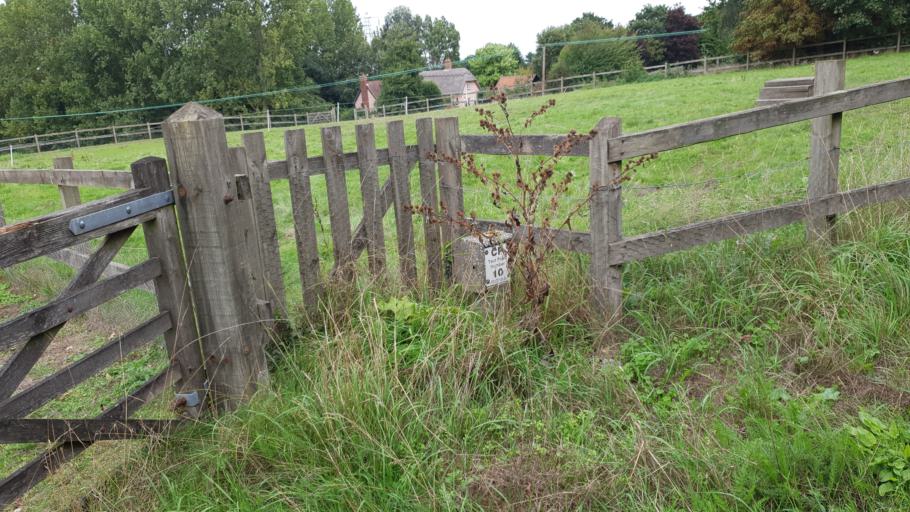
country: GB
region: England
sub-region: Suffolk
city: East Bergholt
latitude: 51.9436
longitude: 1.0238
